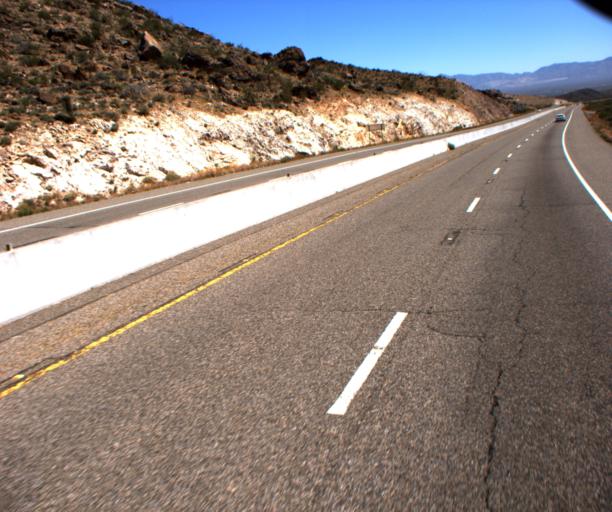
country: US
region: Arizona
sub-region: Mohave County
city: Golden Valley
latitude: 35.2235
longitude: -114.3851
